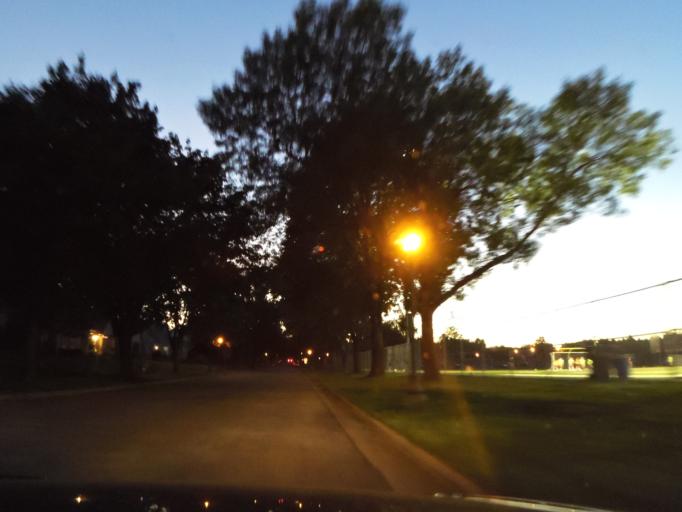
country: US
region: Minnesota
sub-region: Dakota County
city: Mendota Heights
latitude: 44.9233
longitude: -93.1575
